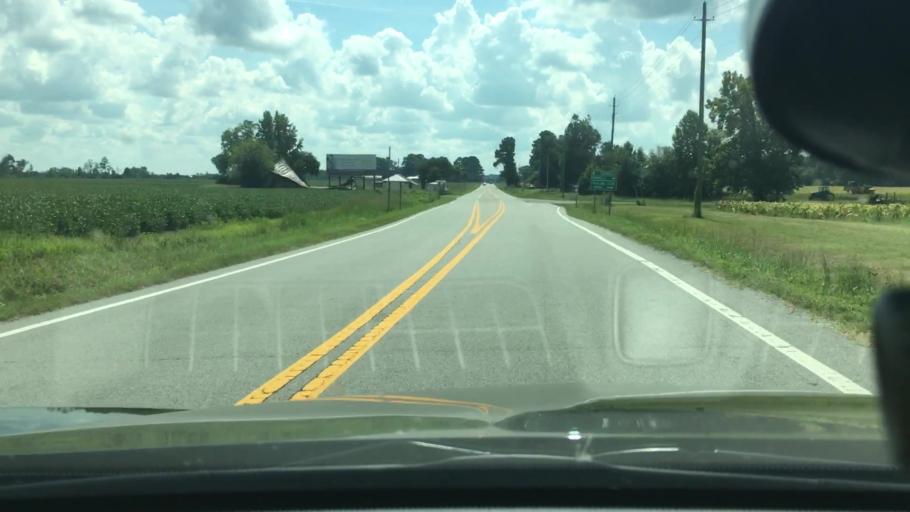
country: US
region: North Carolina
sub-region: Pitt County
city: Farmville
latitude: 35.6742
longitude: -77.4866
